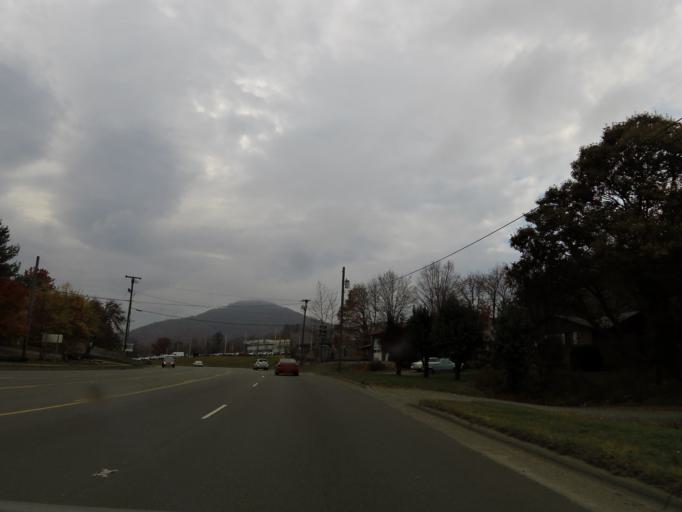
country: US
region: North Carolina
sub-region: Watauga County
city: Boone
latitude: 36.2220
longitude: -81.6506
